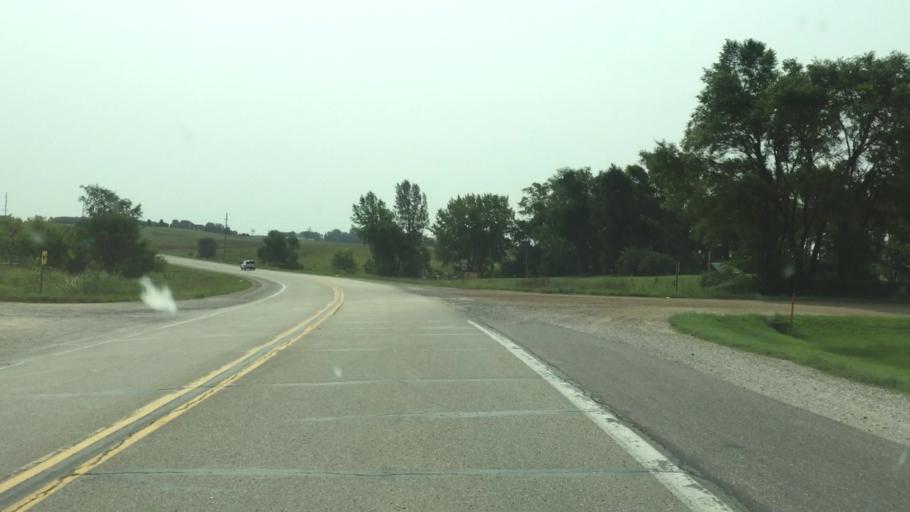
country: US
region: Iowa
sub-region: Dickinson County
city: Milford
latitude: 43.3438
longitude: -95.1780
